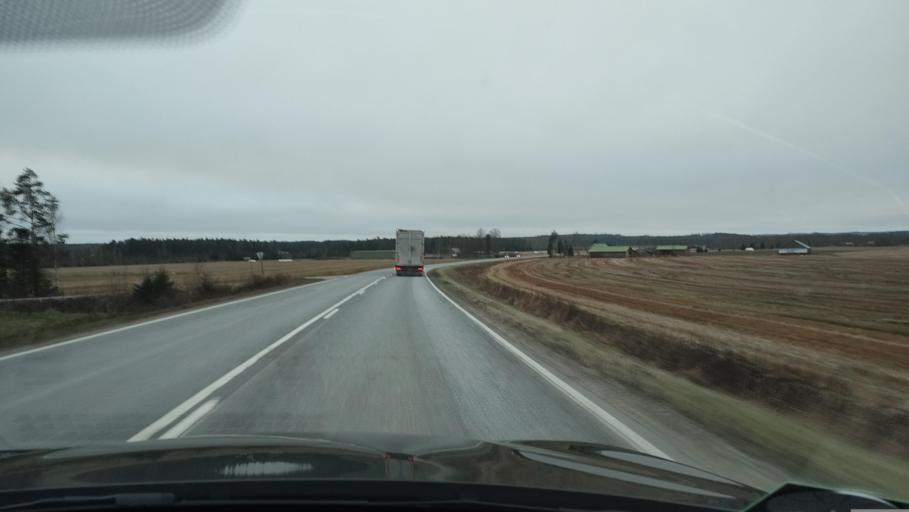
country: FI
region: Southern Ostrobothnia
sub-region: Suupohja
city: Kauhajoki
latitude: 62.3868
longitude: 22.1412
